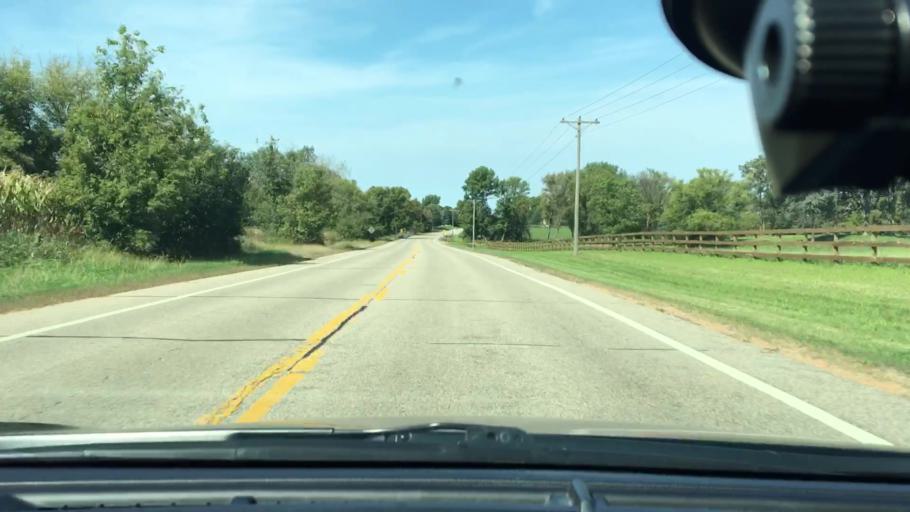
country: US
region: Minnesota
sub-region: Hennepin County
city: Corcoran
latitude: 45.1004
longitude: -93.5549
